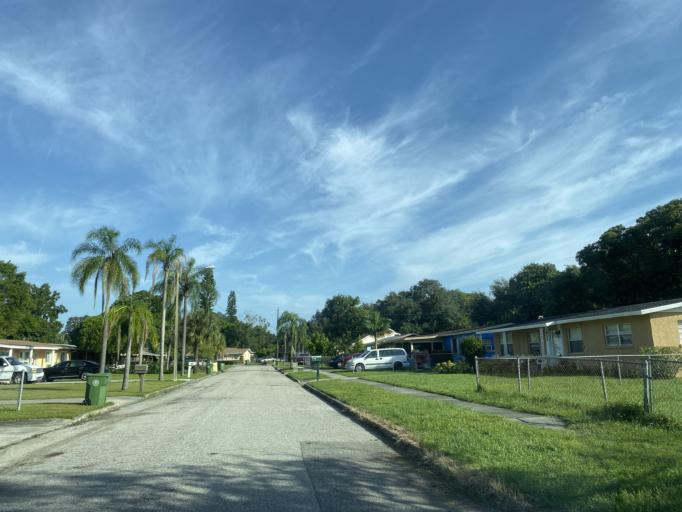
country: US
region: Florida
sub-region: Manatee County
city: Samoset
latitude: 27.4917
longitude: -82.5441
